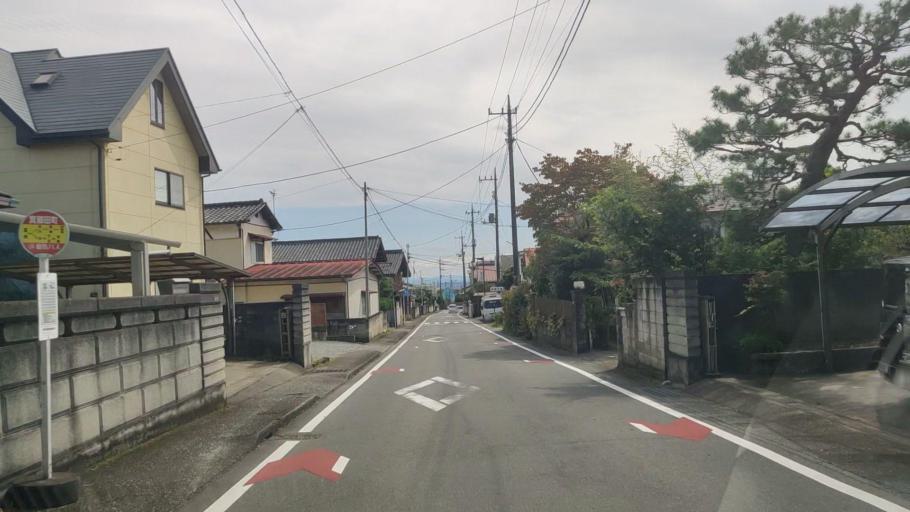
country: JP
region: Gunma
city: Kanekomachi
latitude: 36.3928
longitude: 138.9572
